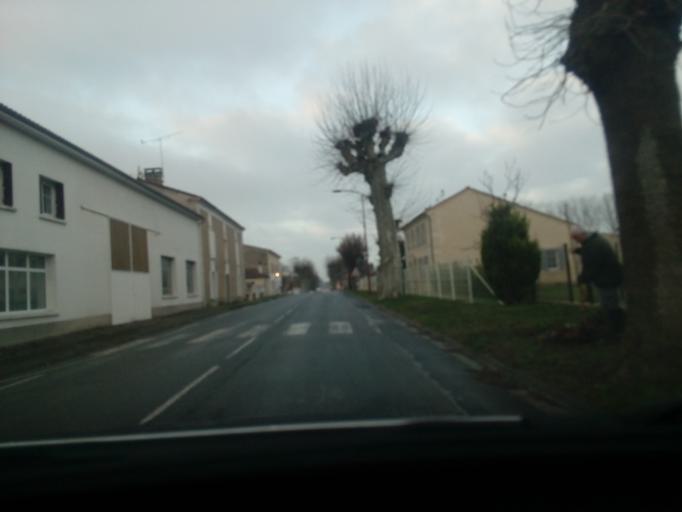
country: FR
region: Poitou-Charentes
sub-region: Departement de la Charente
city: Baignes-Sainte-Radegonde
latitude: 45.4434
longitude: -0.2979
